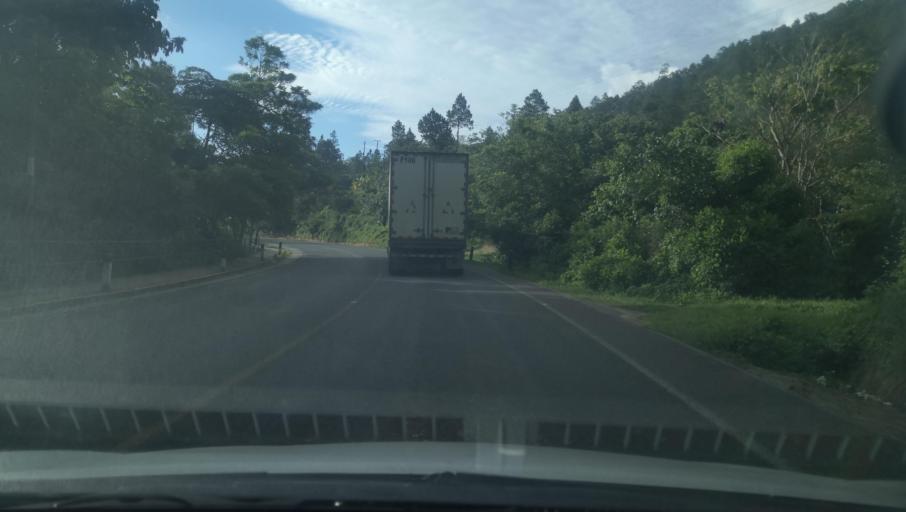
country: NI
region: Nueva Segovia
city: Mozonte
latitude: 13.7297
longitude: -86.5103
